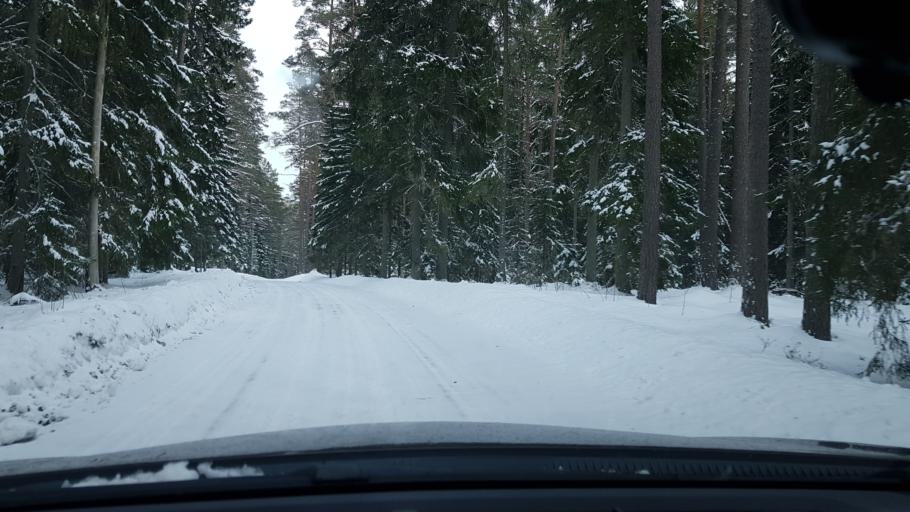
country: EE
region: Laeaene-Virumaa
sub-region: Haljala vald
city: Haljala
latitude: 59.5643
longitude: 26.0850
